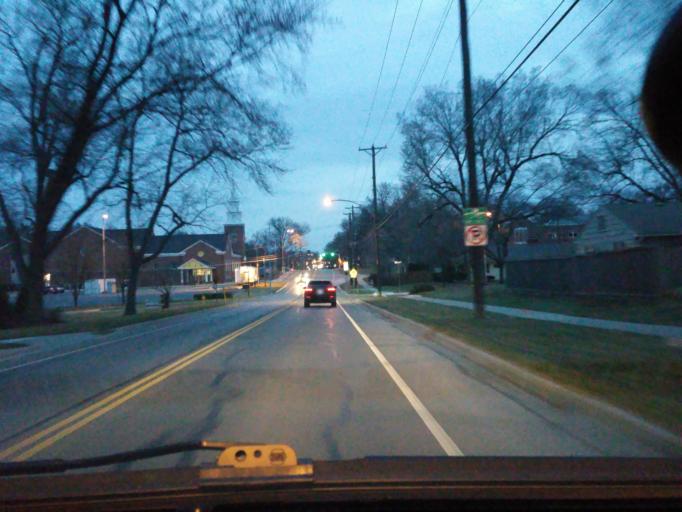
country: US
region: Kansas
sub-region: Johnson County
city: Fairway
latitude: 39.0103
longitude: -94.6305
